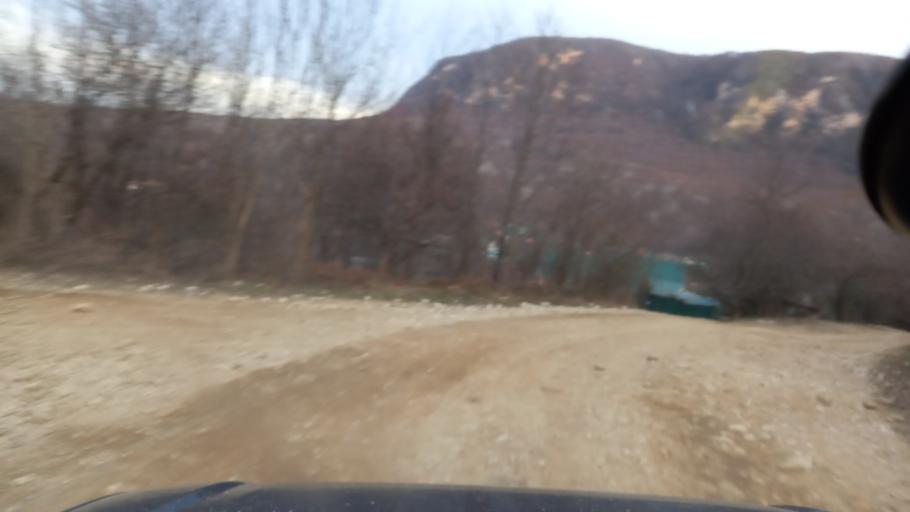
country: RU
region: Krasnodarskiy
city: Neftegorsk
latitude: 44.2284
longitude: 39.8976
